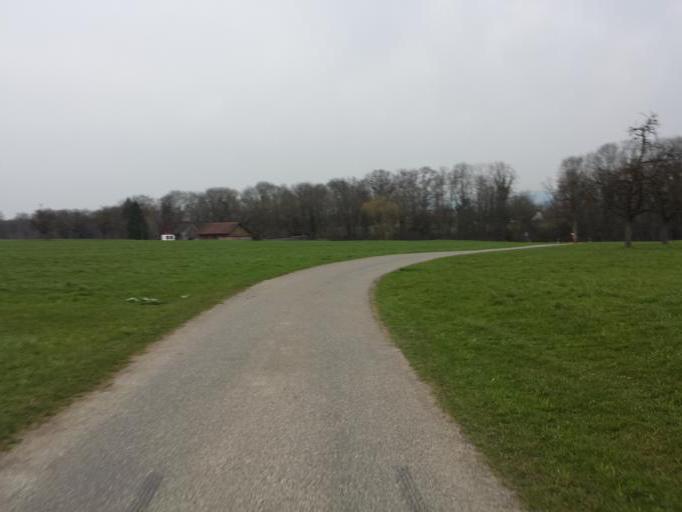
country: CH
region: Thurgau
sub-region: Arbon District
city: Uttwil
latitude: 47.5531
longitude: 9.3365
